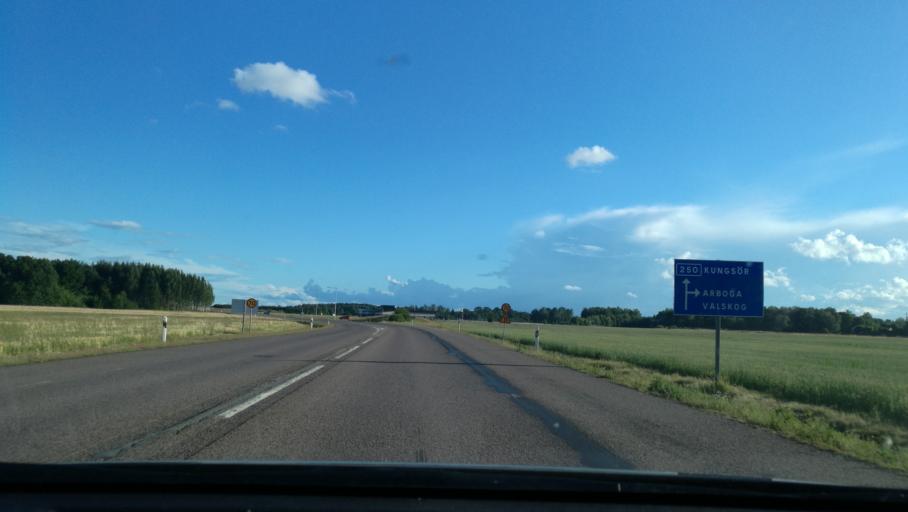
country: SE
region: Vaestmanland
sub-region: Kopings Kommun
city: Koping
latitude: 59.4863
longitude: 15.9854
